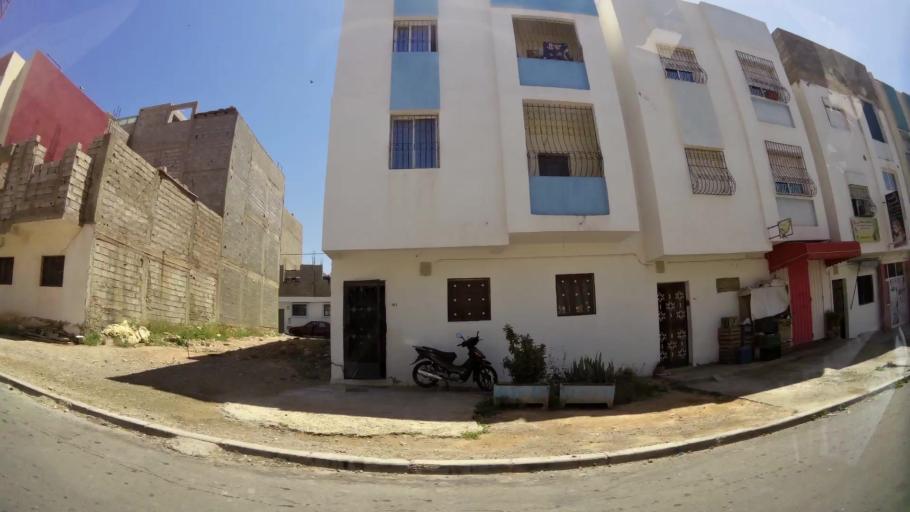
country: MA
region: Oued ed Dahab-Lagouira
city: Dakhla
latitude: 30.4354
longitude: -9.5481
